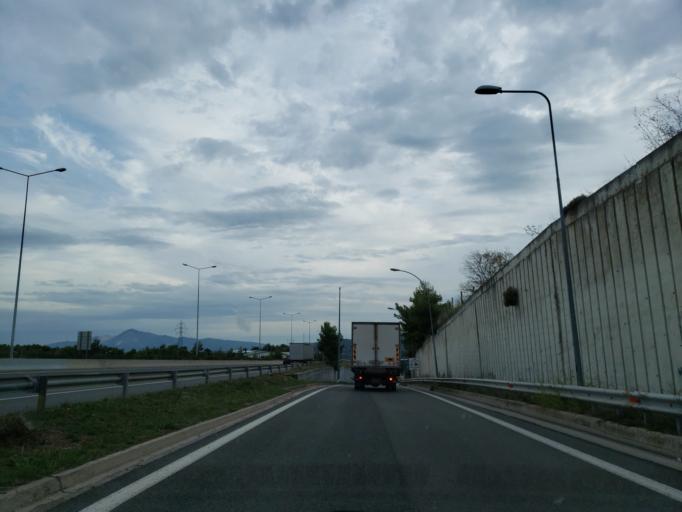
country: GR
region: Attica
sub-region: Nomarchia Anatolikis Attikis
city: Afidnes
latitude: 38.2040
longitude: 23.8545
